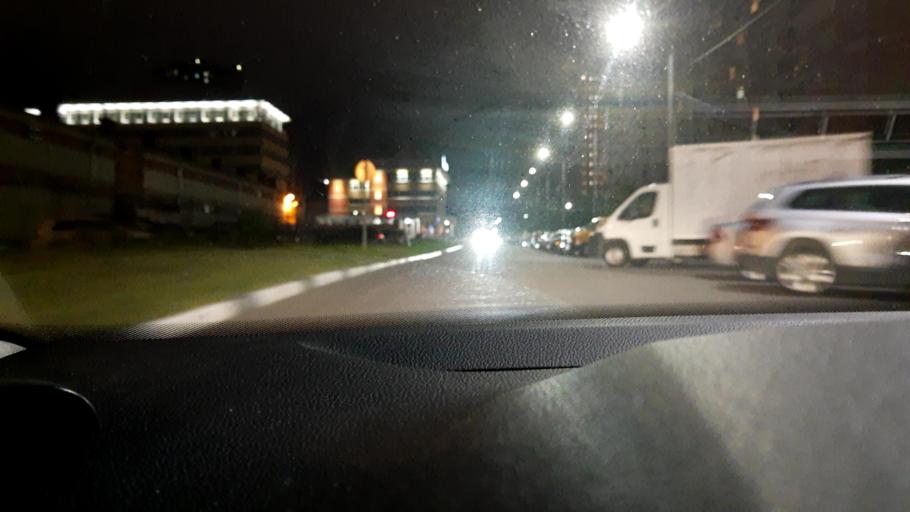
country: RU
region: Moskovskaya
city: Opalikha
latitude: 55.8320
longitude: 37.2920
